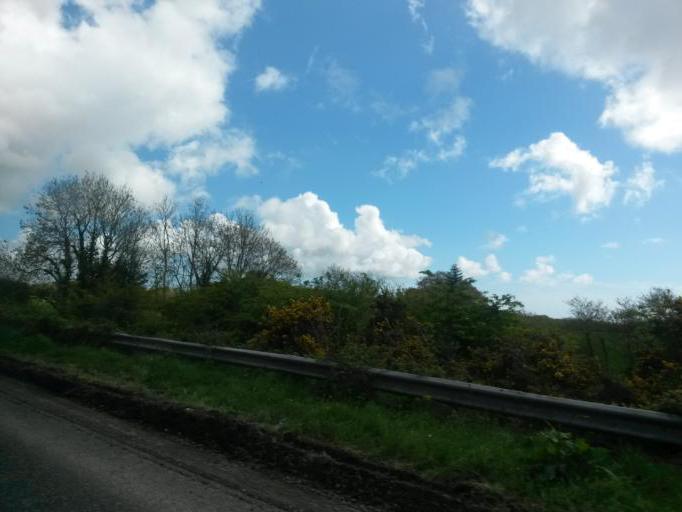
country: IE
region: Leinster
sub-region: Loch Garman
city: Castlebridge
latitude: 52.3801
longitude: -6.5195
